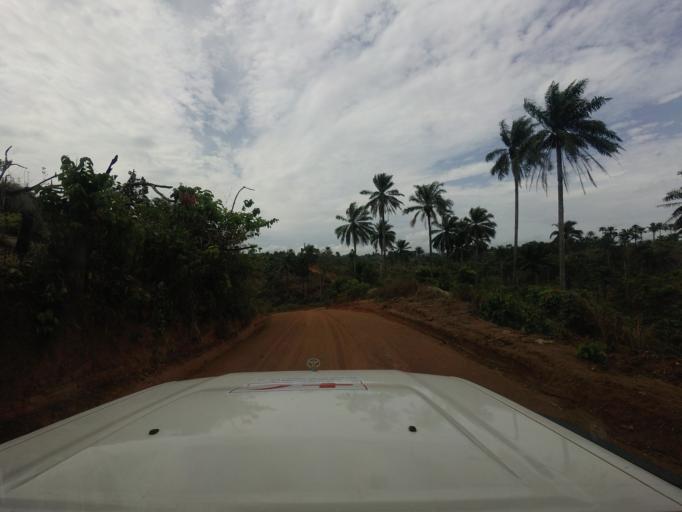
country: SL
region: Eastern Province
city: Buedu
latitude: 8.2197
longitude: -10.2220
